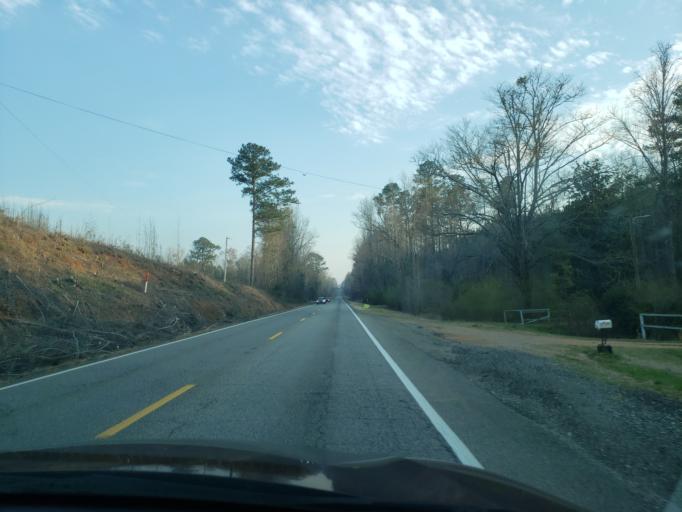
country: US
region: Alabama
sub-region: Hale County
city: Greensboro
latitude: 32.8032
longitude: -87.5933
